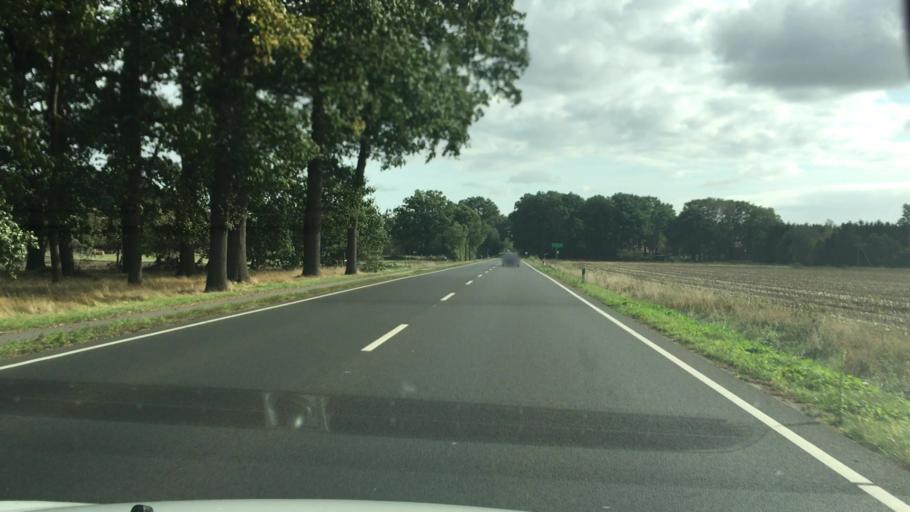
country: DE
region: Lower Saxony
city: Diepholz
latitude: 52.6382
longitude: 8.3508
